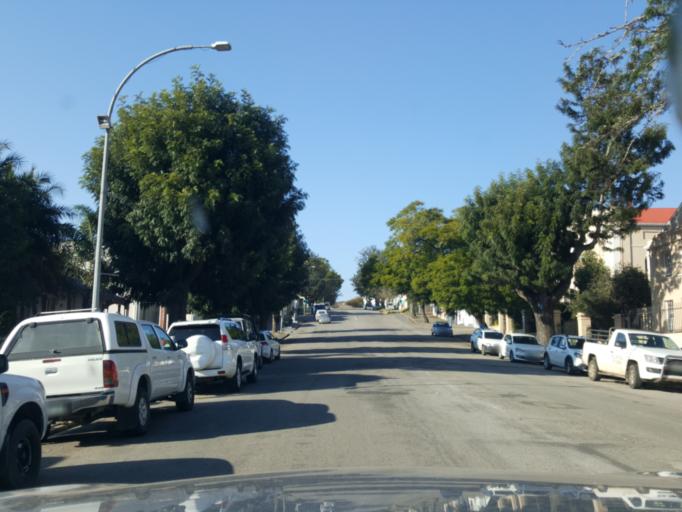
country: ZA
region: Eastern Cape
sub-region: Cacadu District Municipality
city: Grahamstown
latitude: -33.3122
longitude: 26.5281
